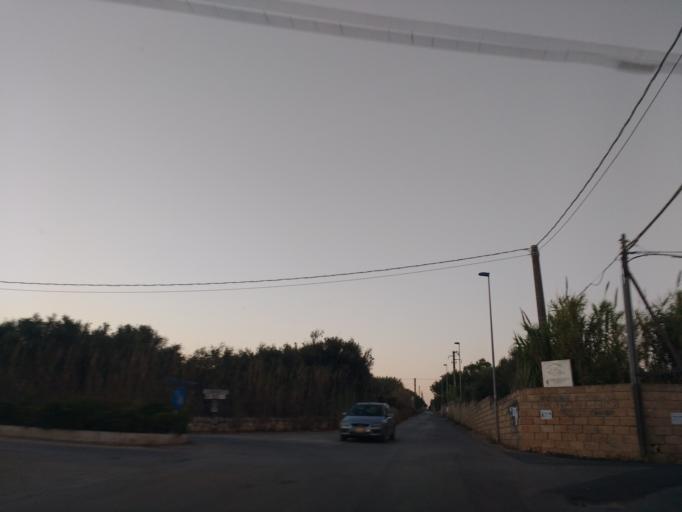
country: IT
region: Sicily
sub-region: Ragusa
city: Cava d'Aliga
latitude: 36.7231
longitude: 14.6960
